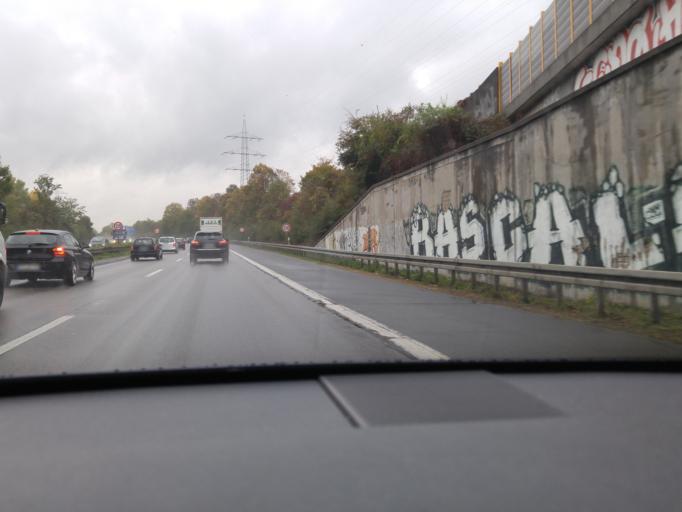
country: DE
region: Hesse
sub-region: Regierungsbezirk Darmstadt
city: Eschborn
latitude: 50.1292
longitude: 8.5718
